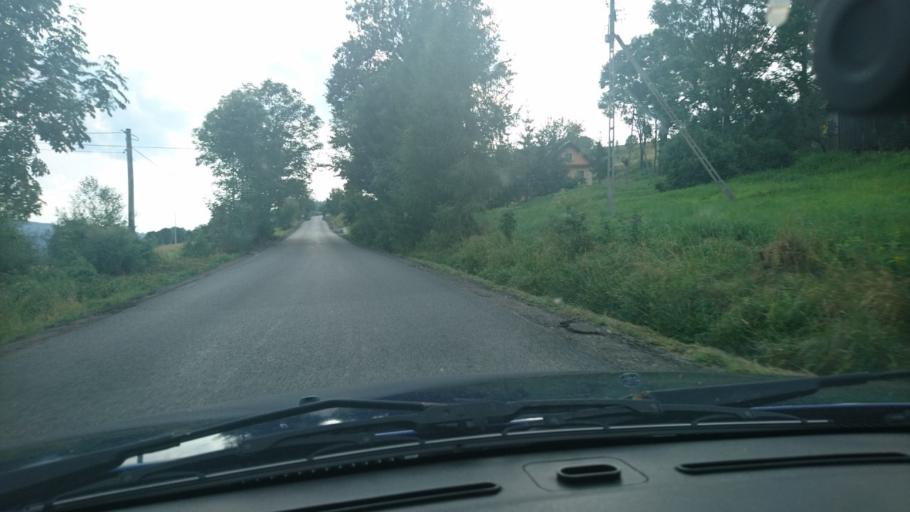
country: PL
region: Silesian Voivodeship
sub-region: Powiat zywiecki
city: Laliki
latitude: 49.5486
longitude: 19.0108
